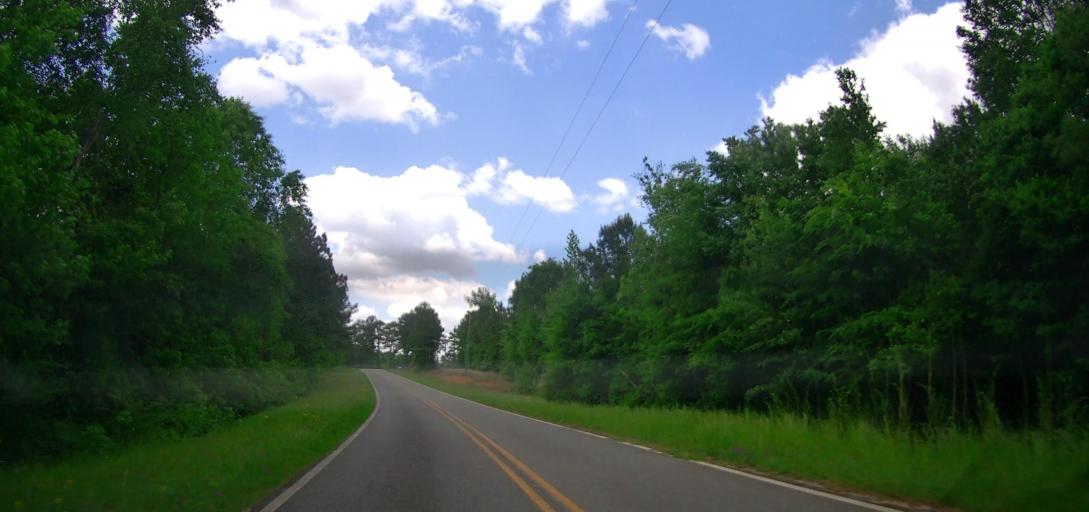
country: US
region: Georgia
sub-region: Laurens County
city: East Dublin
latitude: 32.6131
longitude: -82.8084
